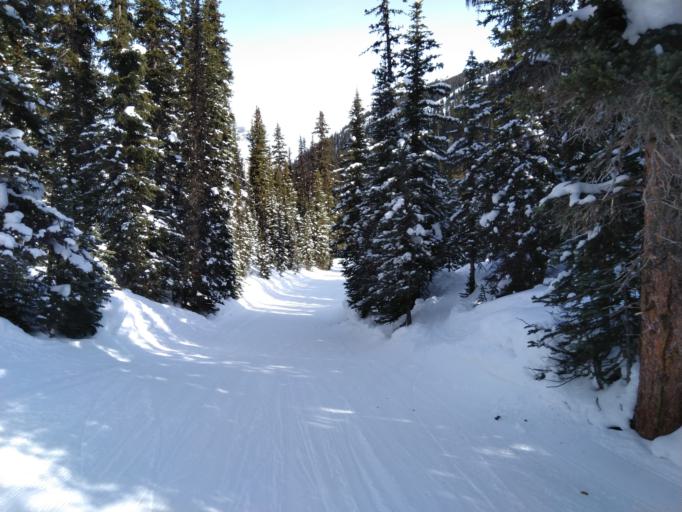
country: CA
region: Alberta
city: Banff
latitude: 51.0877
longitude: -115.7677
